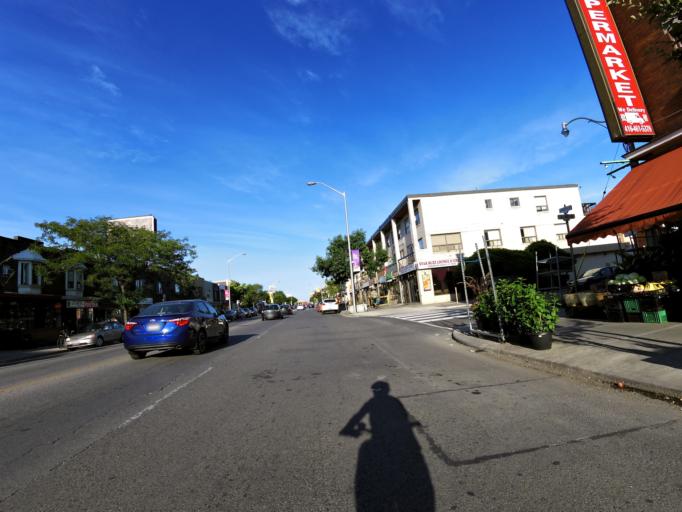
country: CA
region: Ontario
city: Toronto
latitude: 43.6822
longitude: -79.3286
